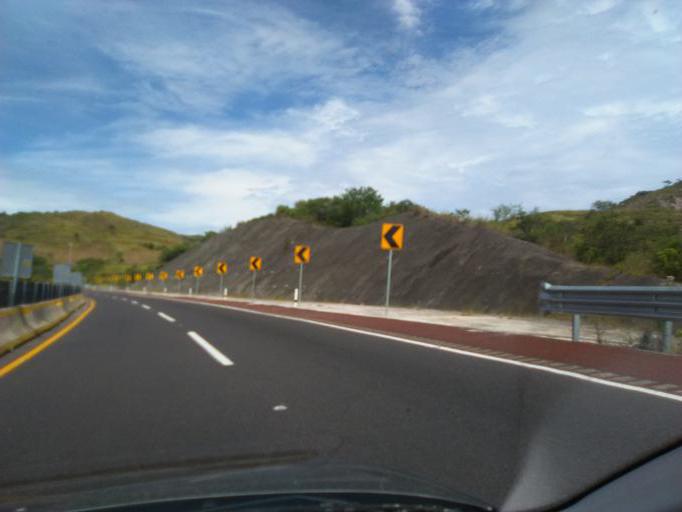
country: MX
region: Guerrero
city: Mazatlan
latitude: 17.4000
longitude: -99.4622
